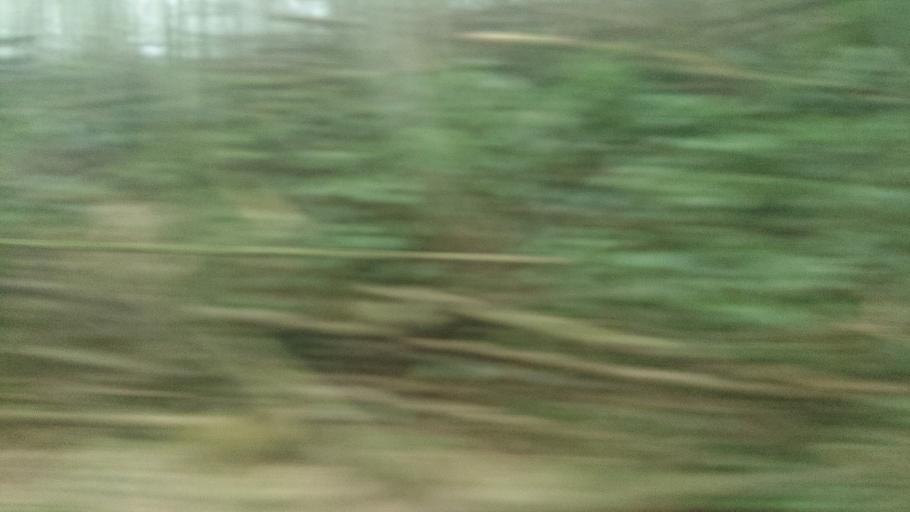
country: TW
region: Taiwan
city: Lugu
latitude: 23.6296
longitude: 120.7159
